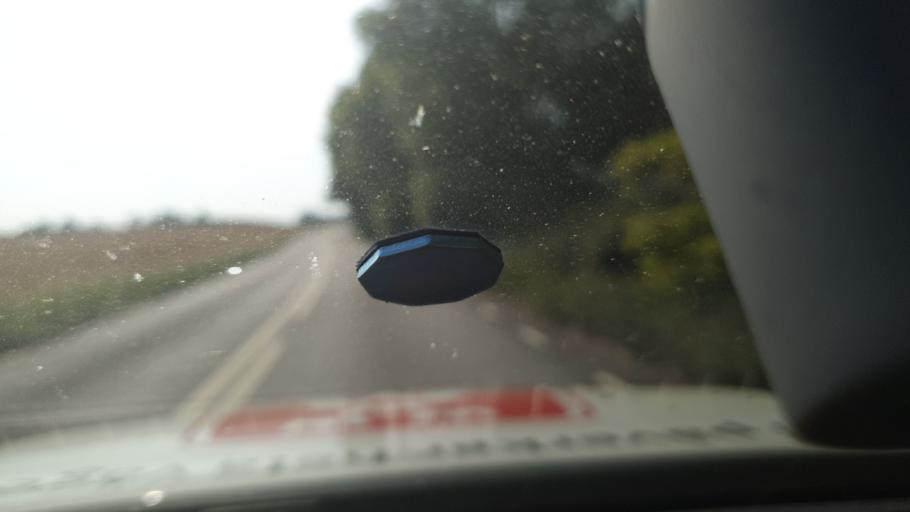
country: SE
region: Skane
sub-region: Svedala Kommun
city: Svedala
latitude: 55.4540
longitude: 13.2269
